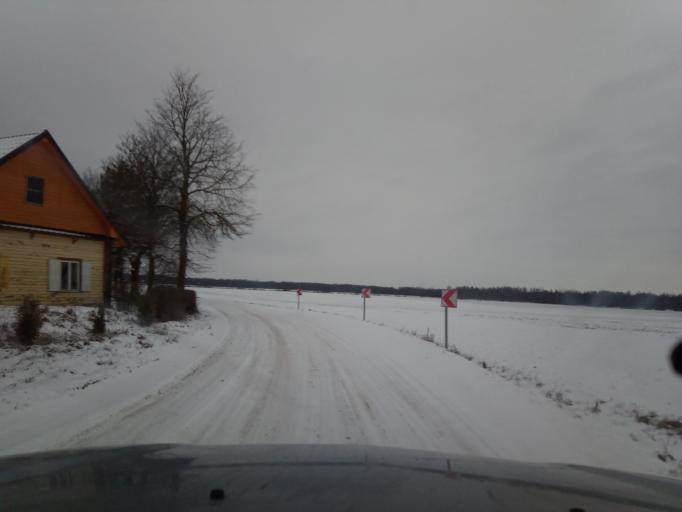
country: LT
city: Ramygala
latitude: 55.4863
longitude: 24.5827
